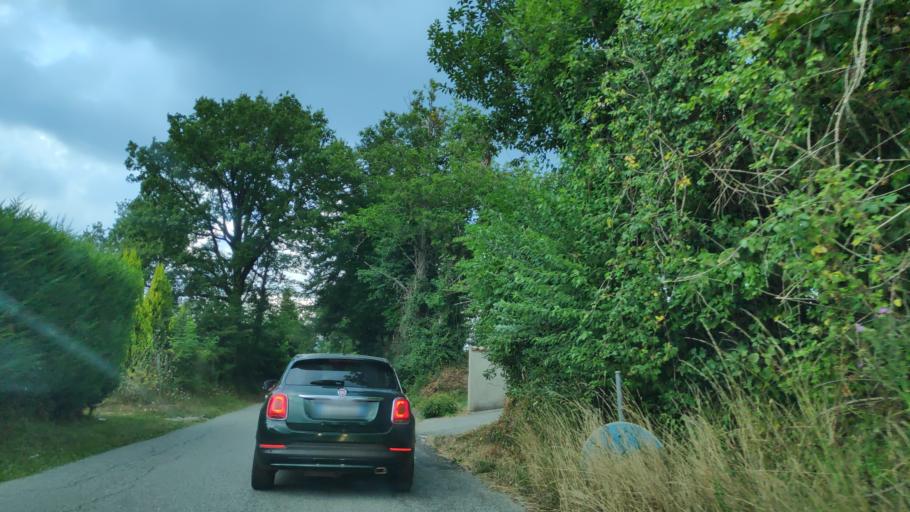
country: IT
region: Calabria
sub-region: Provincia di Vibo-Valentia
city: Serra San Bruno
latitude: 38.5602
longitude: 16.3263
